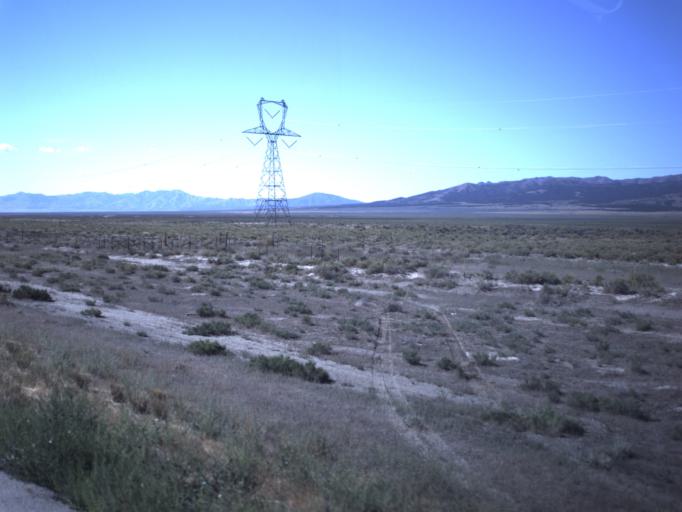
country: US
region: Utah
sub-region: Tooele County
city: Tooele
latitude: 40.3123
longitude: -112.4048
